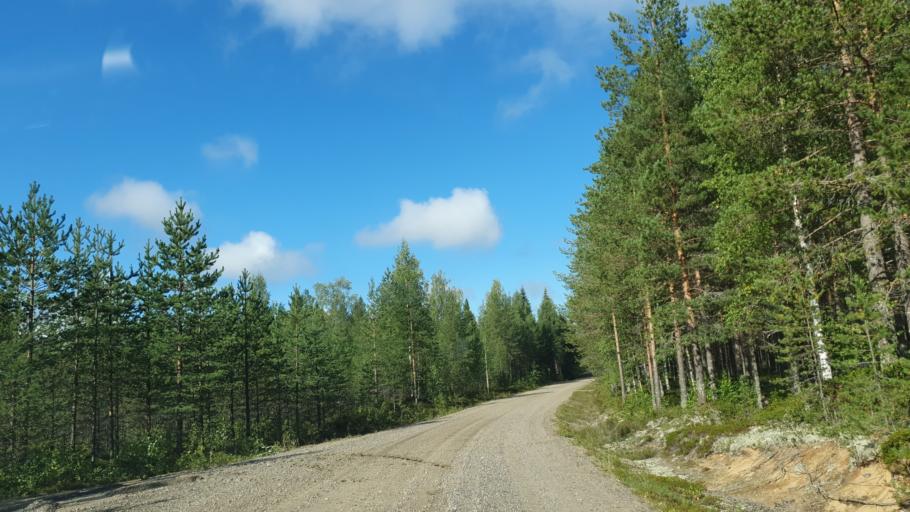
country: FI
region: Kainuu
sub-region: Kehys-Kainuu
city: Kuhmo
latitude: 64.0338
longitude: 29.1645
